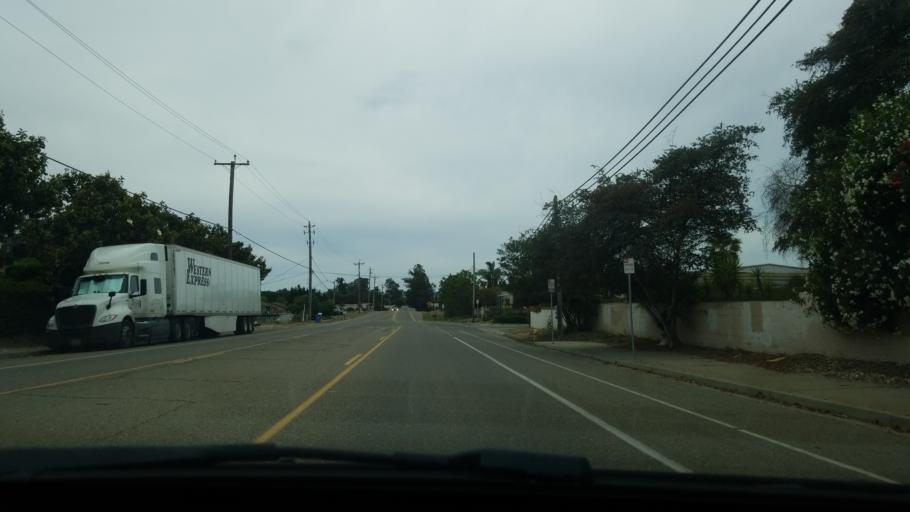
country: US
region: California
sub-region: San Luis Obispo County
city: Nipomo
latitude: 35.0198
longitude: -120.4900
